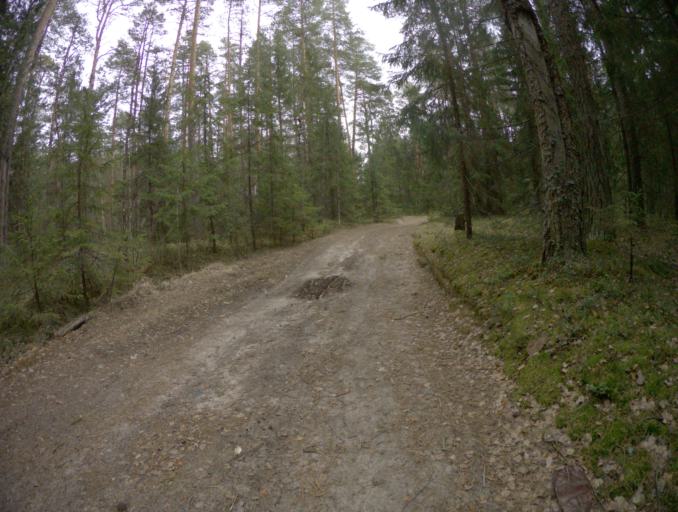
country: RU
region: Vladimir
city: Raduzhnyy
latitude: 55.9495
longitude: 40.2629
